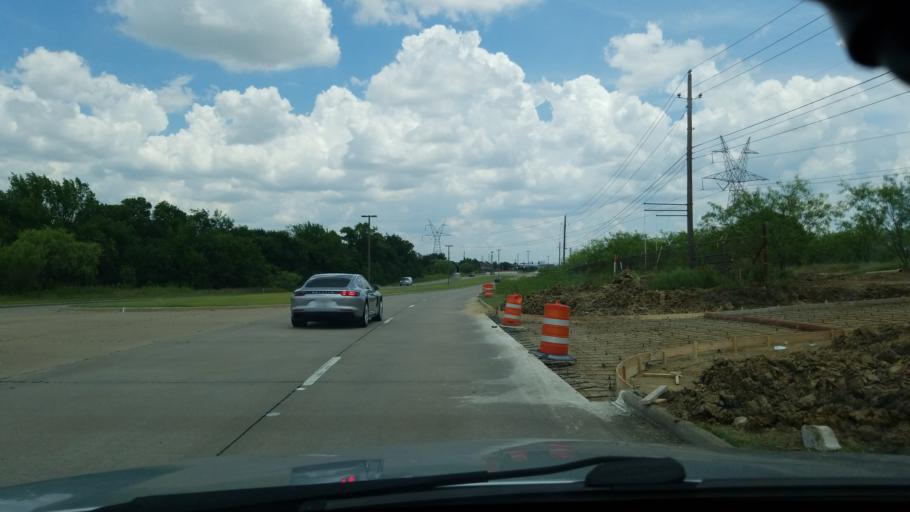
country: US
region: Texas
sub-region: Dallas County
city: Coppell
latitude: 32.9553
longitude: -96.9726
